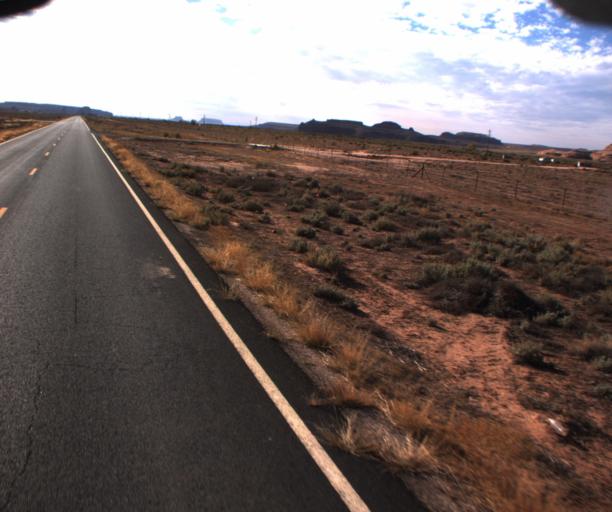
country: US
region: Arizona
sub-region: Apache County
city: Many Farms
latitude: 36.7489
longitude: -109.6423
